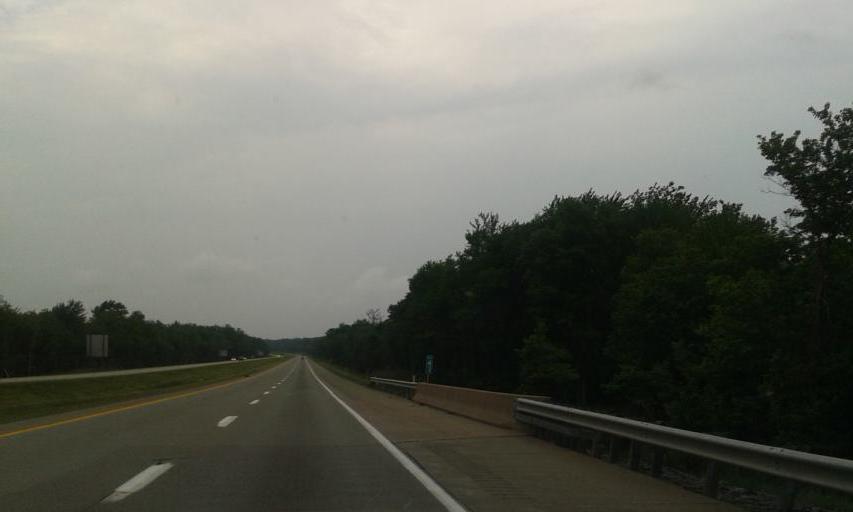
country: US
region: Pennsylvania
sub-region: Monroe County
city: Mount Pocono
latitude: 41.1277
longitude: -75.4001
